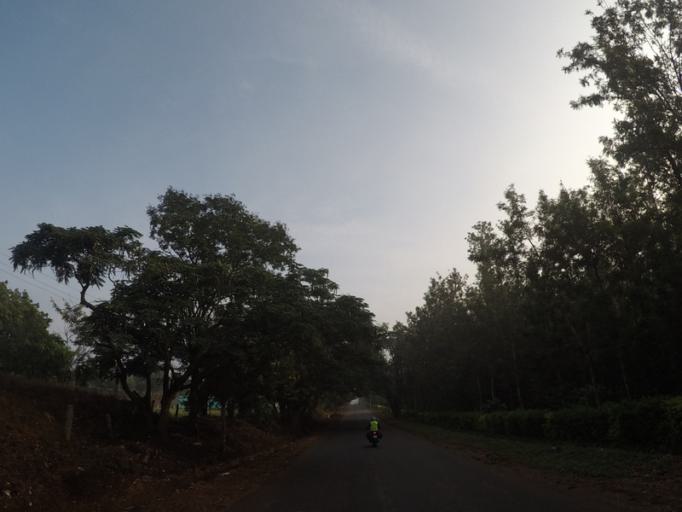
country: IN
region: Karnataka
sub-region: Chikmagalur
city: Chikmagalur
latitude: 13.4120
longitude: 75.7975
